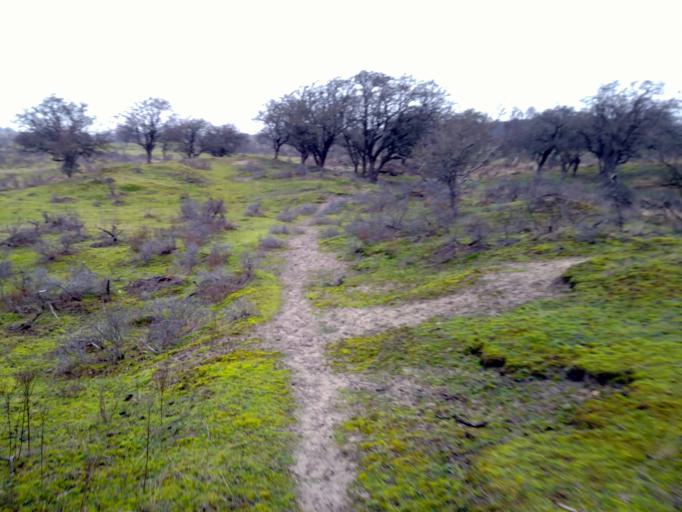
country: NL
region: North Holland
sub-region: Gemeente Zandvoort
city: Zandvoort
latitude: 52.3233
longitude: 4.5372
